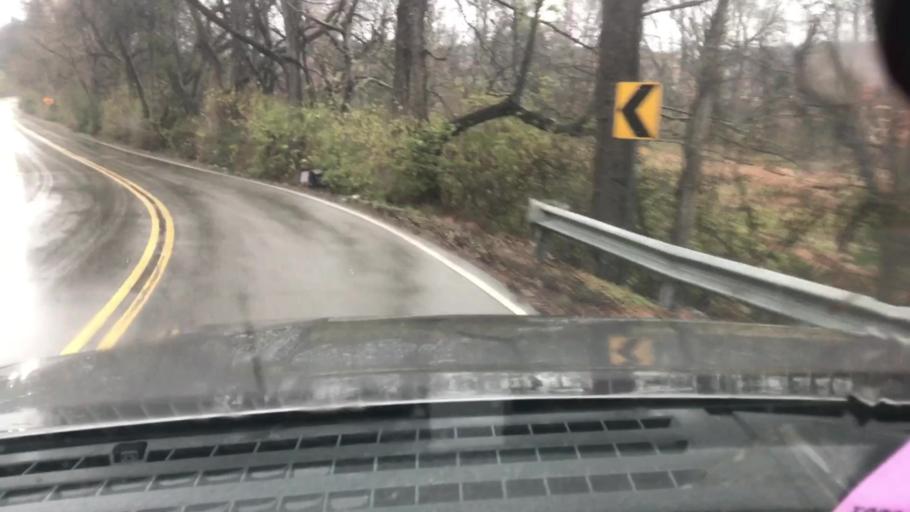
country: US
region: Tennessee
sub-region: Williamson County
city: Brentwood Estates
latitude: 36.0139
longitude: -86.7383
